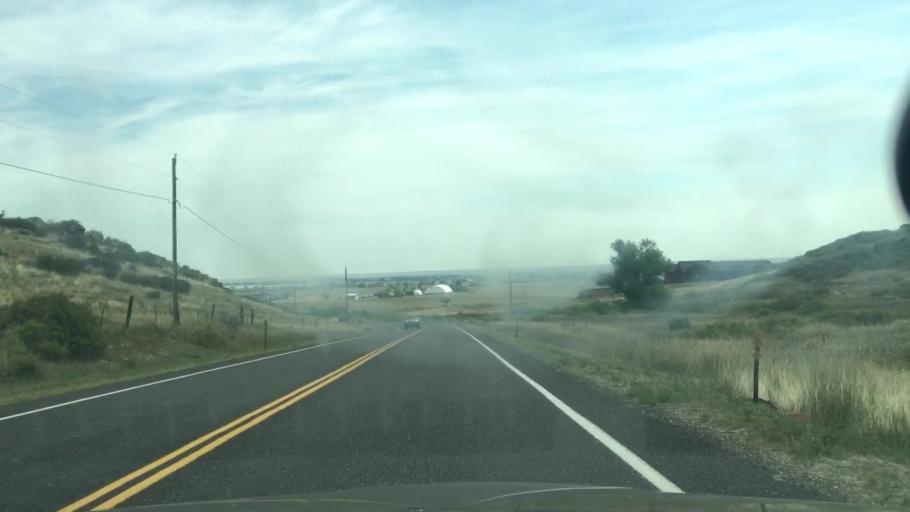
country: US
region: Colorado
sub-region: Larimer County
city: Campion
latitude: 40.3378
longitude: -105.1798
